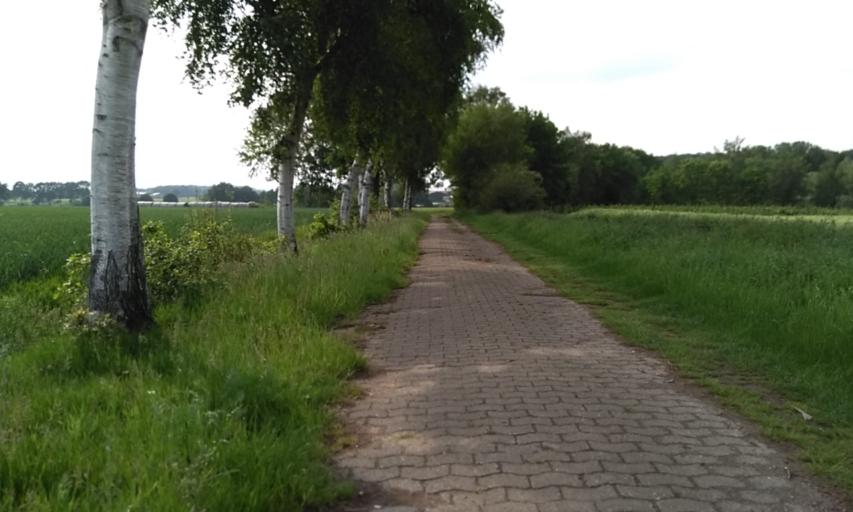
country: DE
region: Lower Saxony
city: Nottensdorf
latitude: 53.4659
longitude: 9.6249
